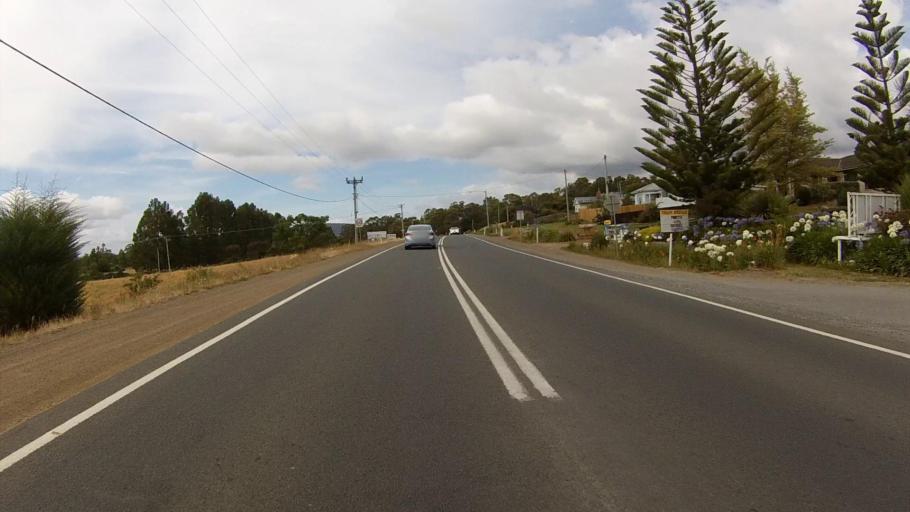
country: AU
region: Tasmania
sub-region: Kingborough
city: Margate
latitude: -43.0356
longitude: 147.2663
